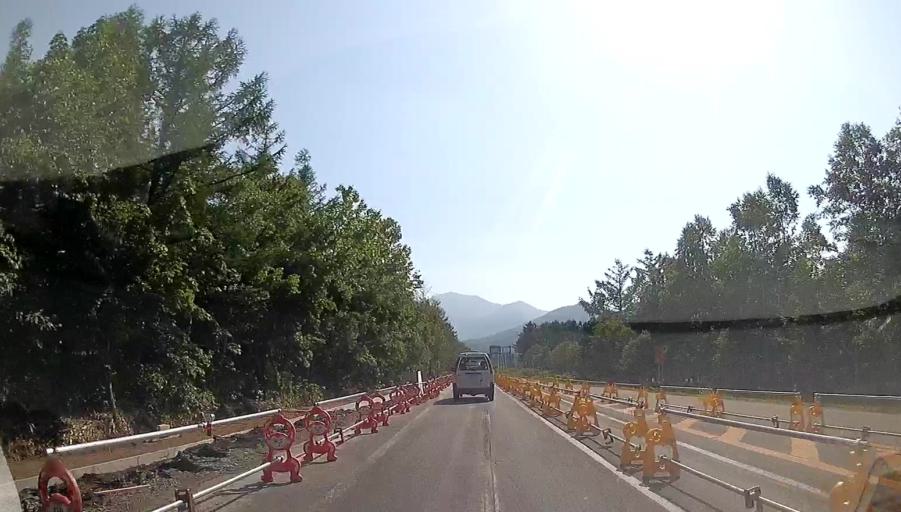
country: JP
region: Hokkaido
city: Otofuke
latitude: 42.9791
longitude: 142.8292
